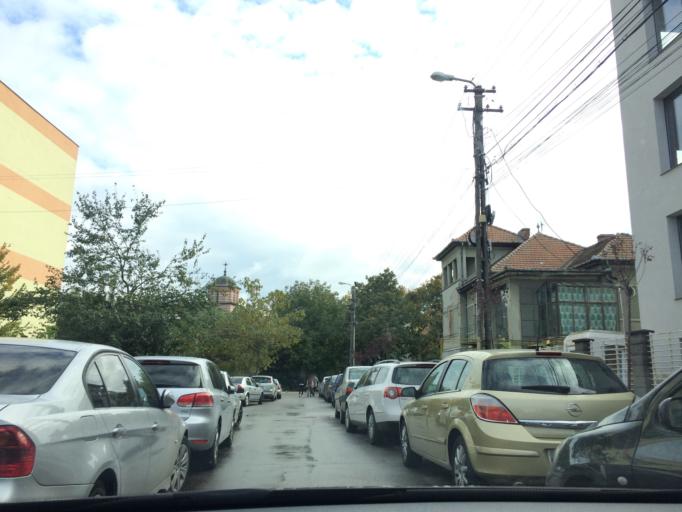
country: RO
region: Timis
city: Timisoara
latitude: 45.7469
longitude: 21.2328
